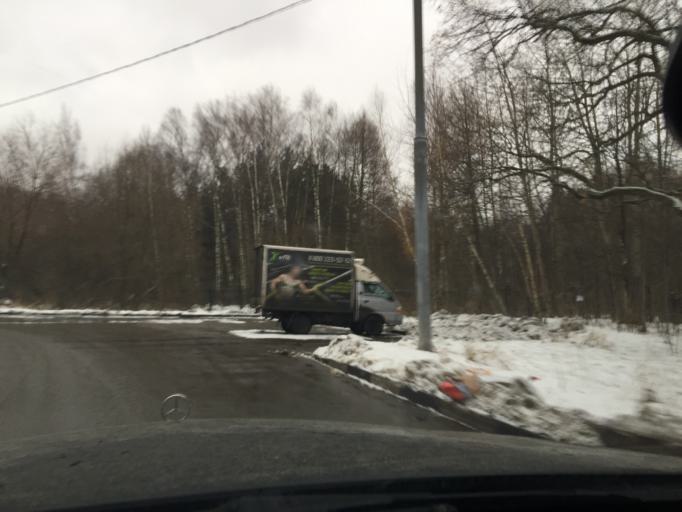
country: RU
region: Moscow
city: Troparevo
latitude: 55.6400
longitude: 37.4749
